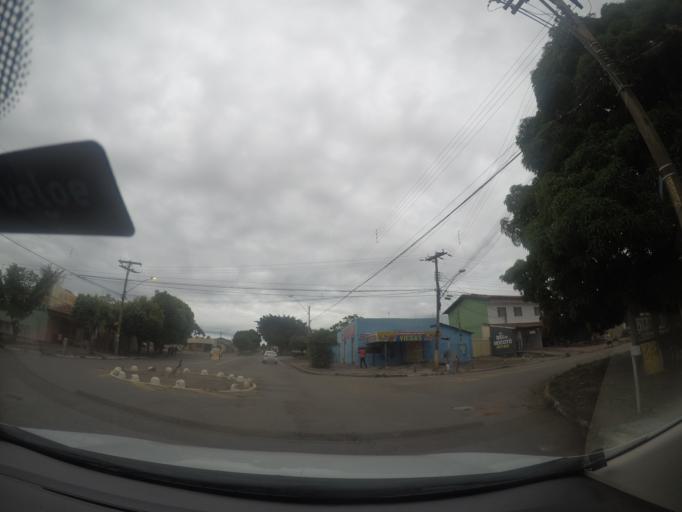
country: BR
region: Goias
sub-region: Goiania
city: Goiania
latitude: -16.6148
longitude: -49.2973
